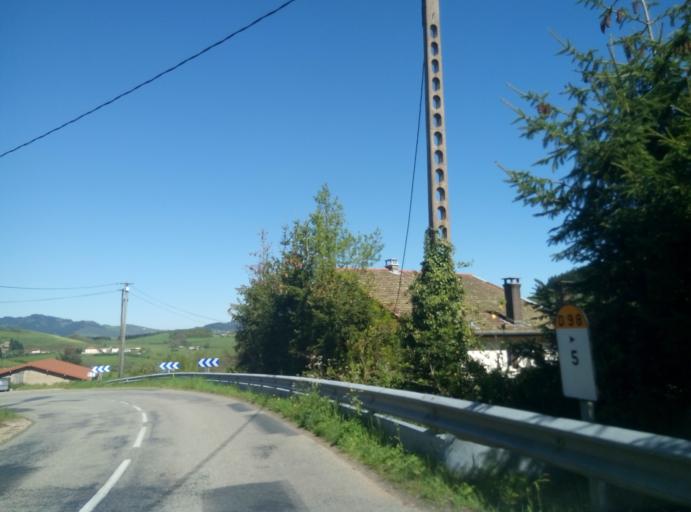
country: FR
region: Rhone-Alpes
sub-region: Departement du Rhone
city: Grandris
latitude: 46.0024
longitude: 4.4535
